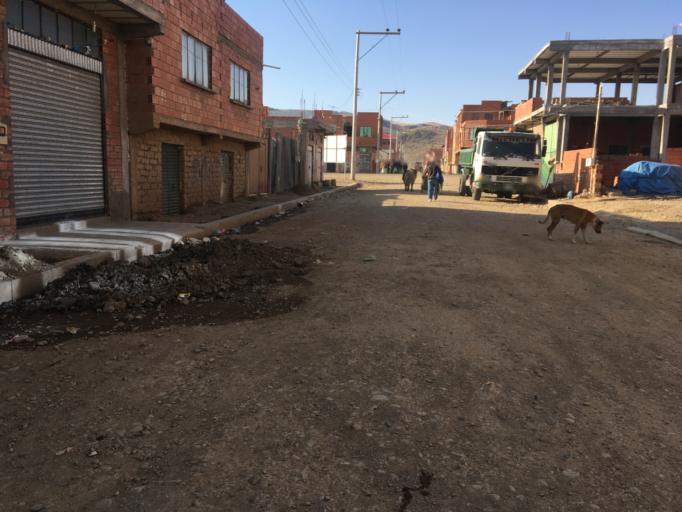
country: BO
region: La Paz
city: Huatajata
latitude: -16.1908
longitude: -68.7444
